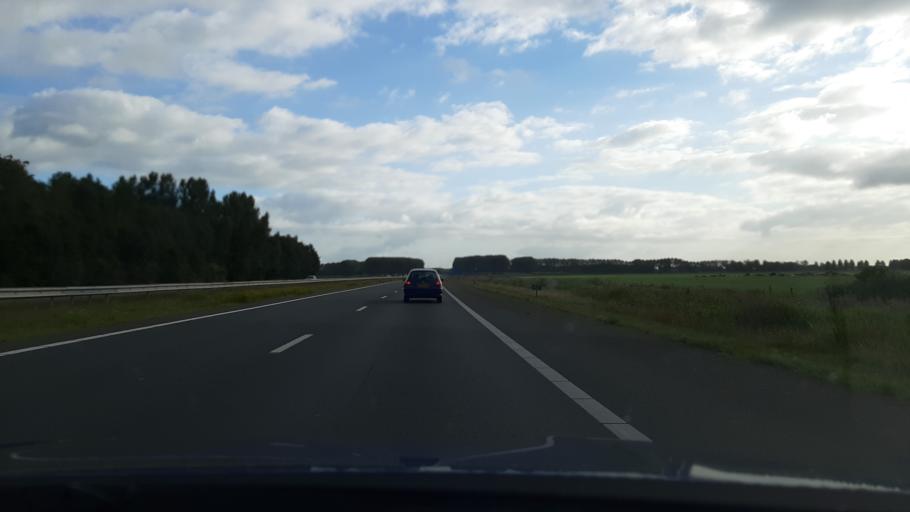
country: NL
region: Friesland
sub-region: Gemeente Opsterland
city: Tijnje
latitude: 53.0109
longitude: 6.0012
